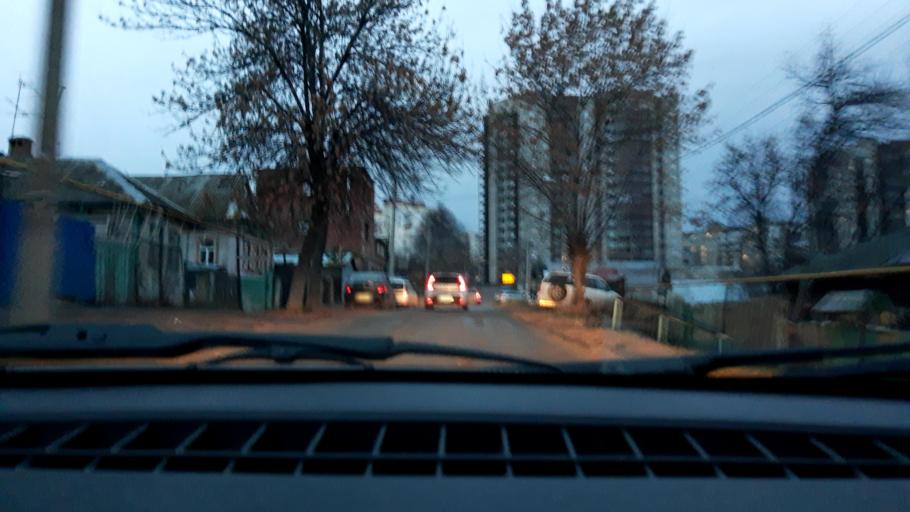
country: RU
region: Bashkortostan
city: Ufa
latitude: 54.7741
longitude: 56.0411
